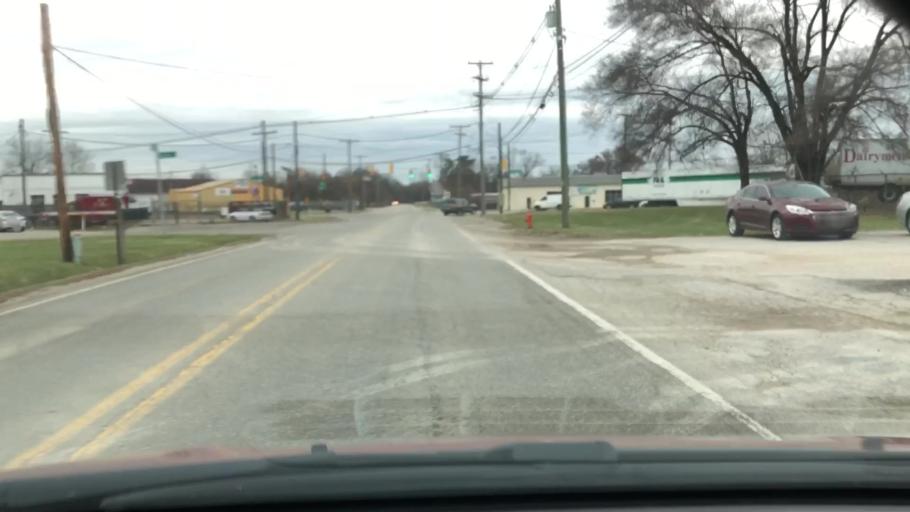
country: US
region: Ohio
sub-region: Franklin County
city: Bexley
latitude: 39.9961
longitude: -82.9294
